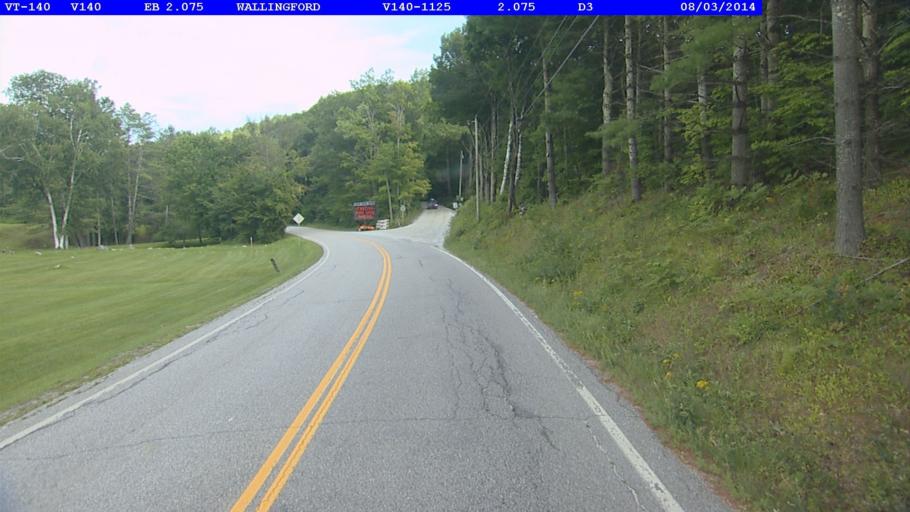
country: US
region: Vermont
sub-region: Rutland County
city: Rutland
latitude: 43.4560
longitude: -72.9452
